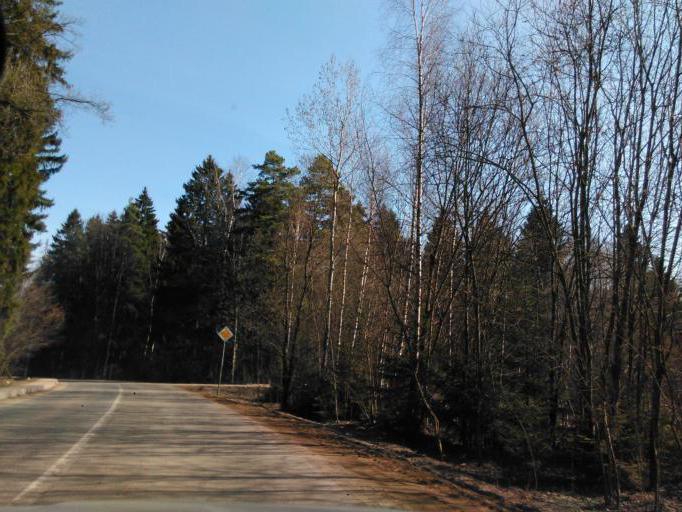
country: RU
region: Moskovskaya
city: Skhodnya
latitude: 55.8902
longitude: 37.2683
